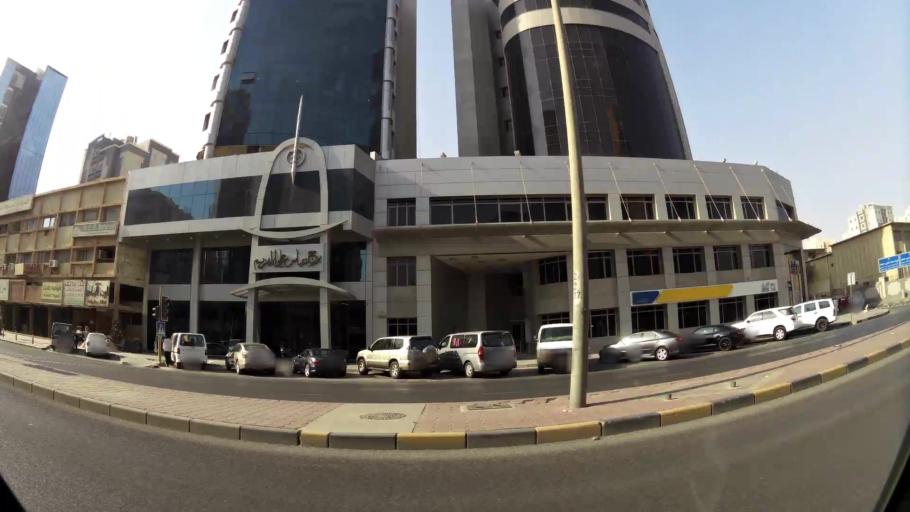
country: KW
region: Muhafazat Hawalli
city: Hawalli
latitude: 29.3428
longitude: 48.0181
